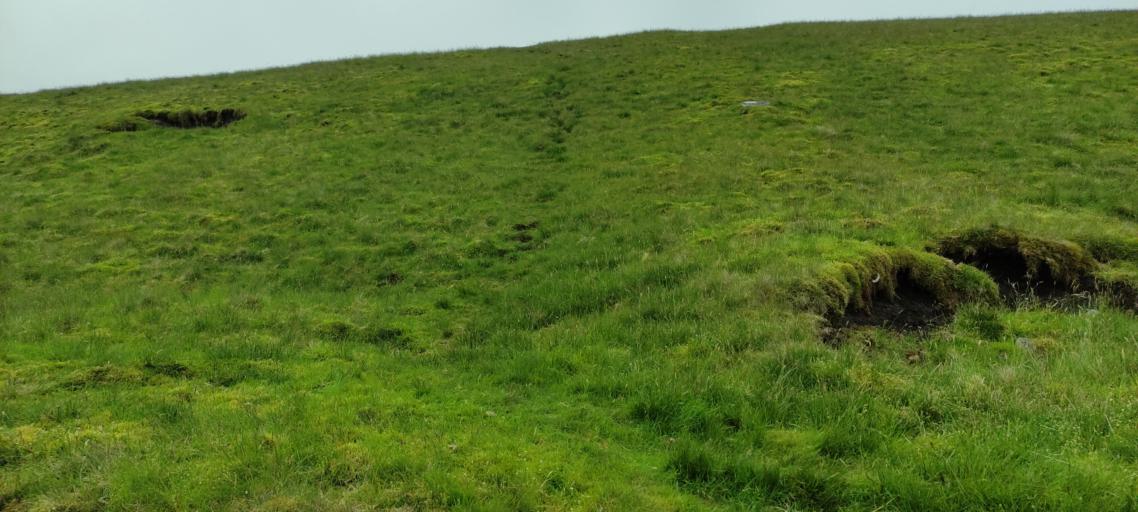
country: GB
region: England
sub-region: Cumbria
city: Kirkby Stephen
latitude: 54.3571
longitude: -2.3673
